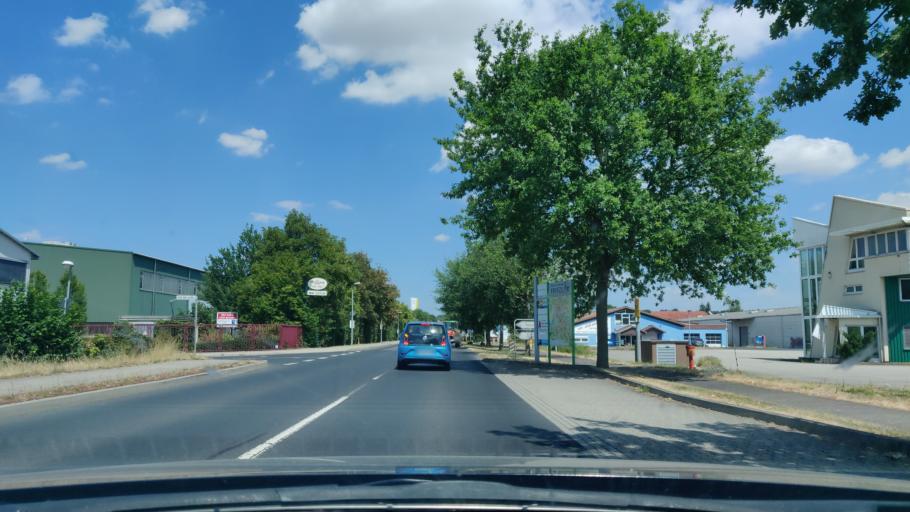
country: DE
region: Hesse
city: Fritzlar
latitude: 51.1213
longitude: 9.2784
